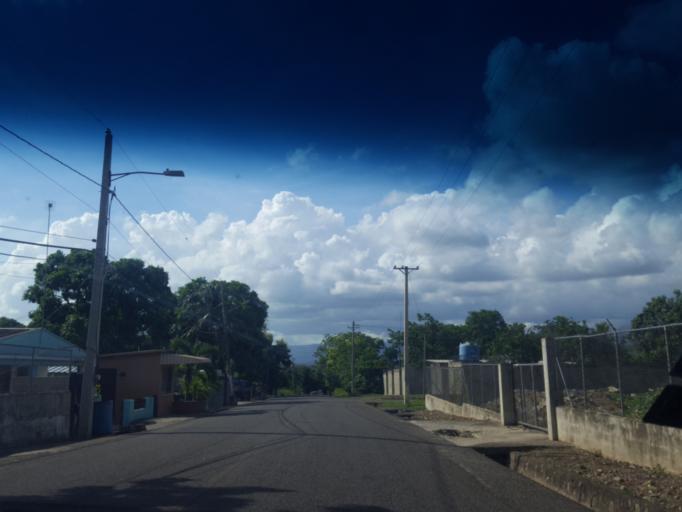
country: DO
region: Santiago
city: Licey al Medio
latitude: 19.3726
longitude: -70.6081
